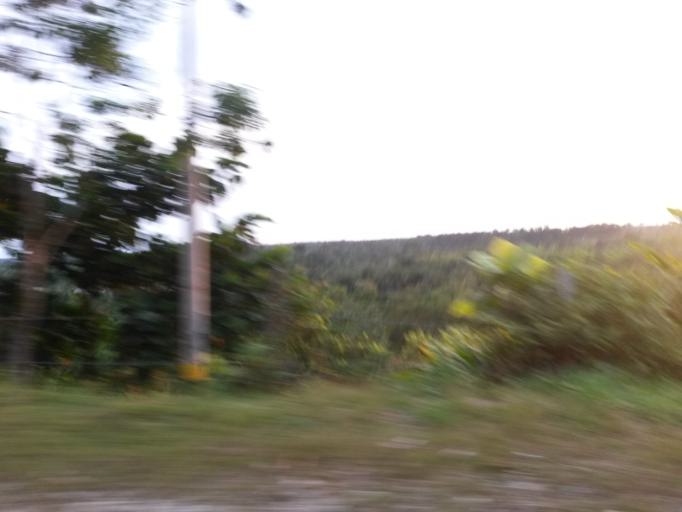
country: CO
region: Putumayo
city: Puerto Guzman
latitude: 1.1372
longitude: -76.2763
